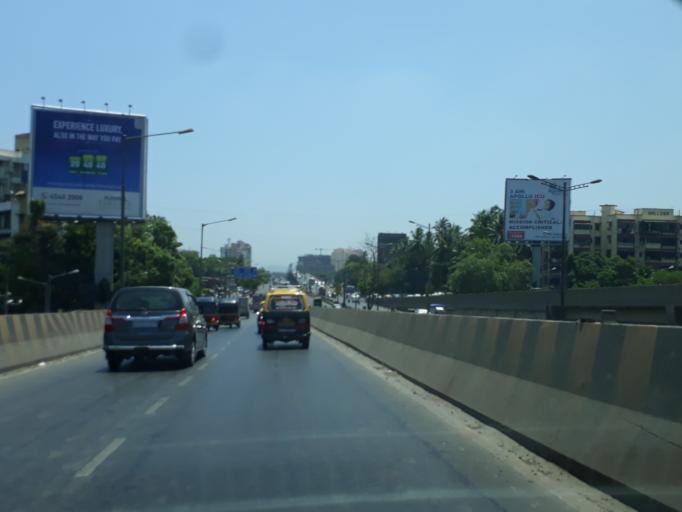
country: IN
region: Maharashtra
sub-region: Mumbai Suburban
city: Mumbai
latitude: 19.0678
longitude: 72.9024
